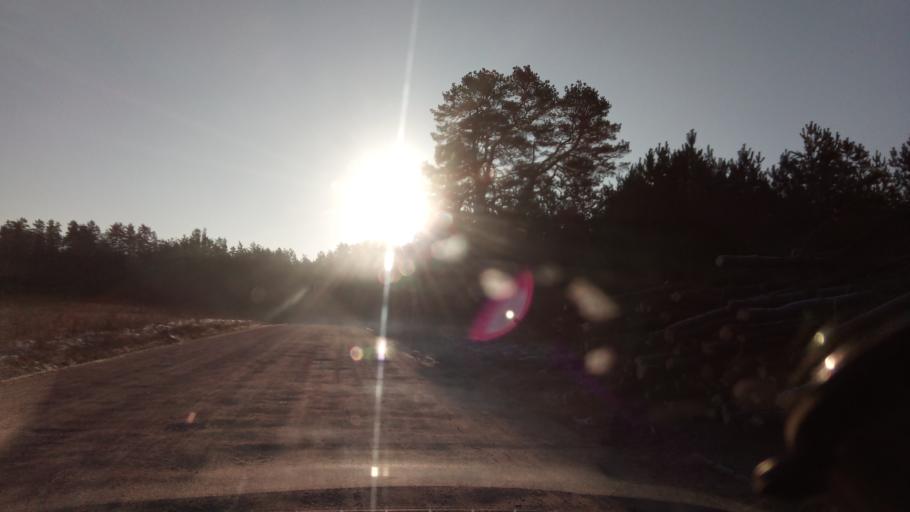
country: LT
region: Alytaus apskritis
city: Druskininkai
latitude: 54.1489
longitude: 23.9359
